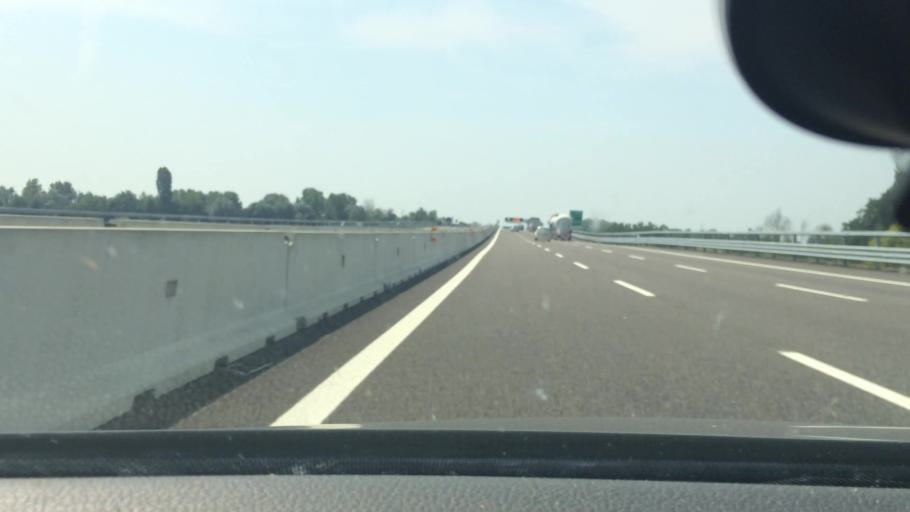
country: IT
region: Lombardy
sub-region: Provincia di Lodi
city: Merlino
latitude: 45.4472
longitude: 9.4278
